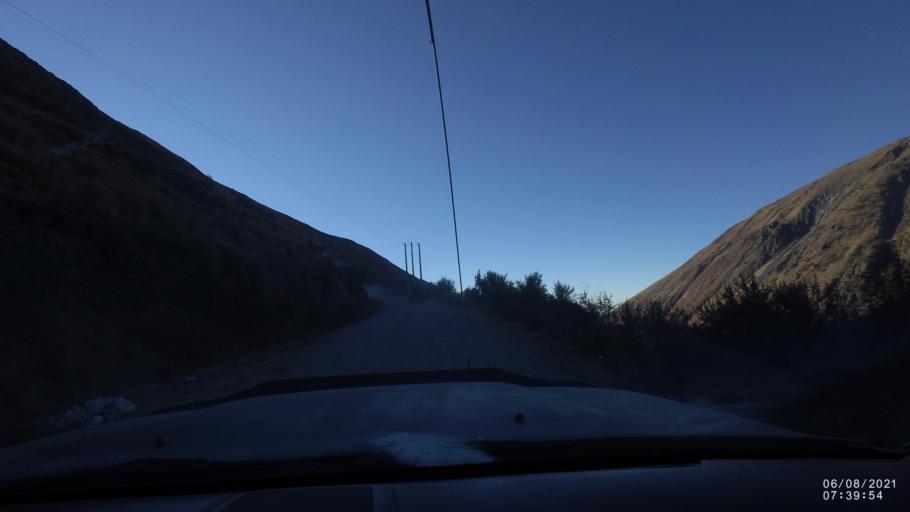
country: BO
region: Cochabamba
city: Sipe Sipe
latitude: -17.2674
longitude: -66.3426
